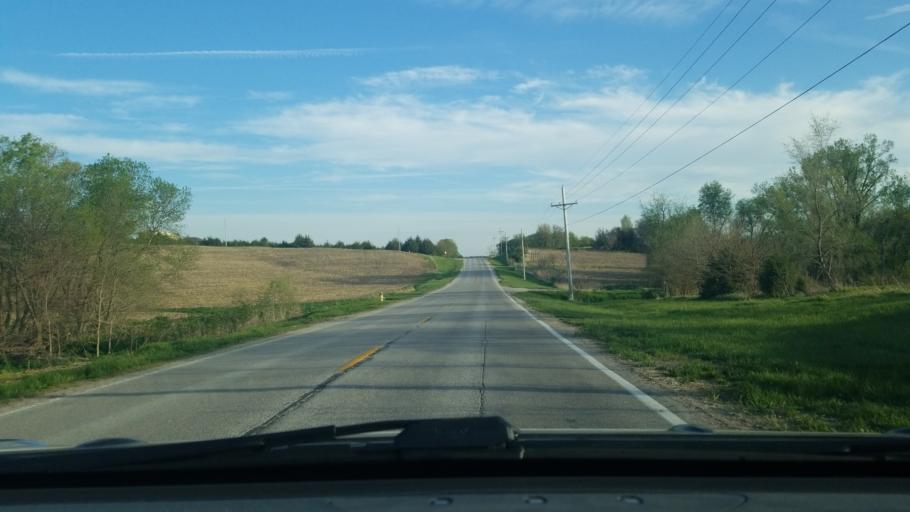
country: US
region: Nebraska
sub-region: Sarpy County
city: Offutt Air Force Base
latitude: 41.0810
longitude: -95.9665
